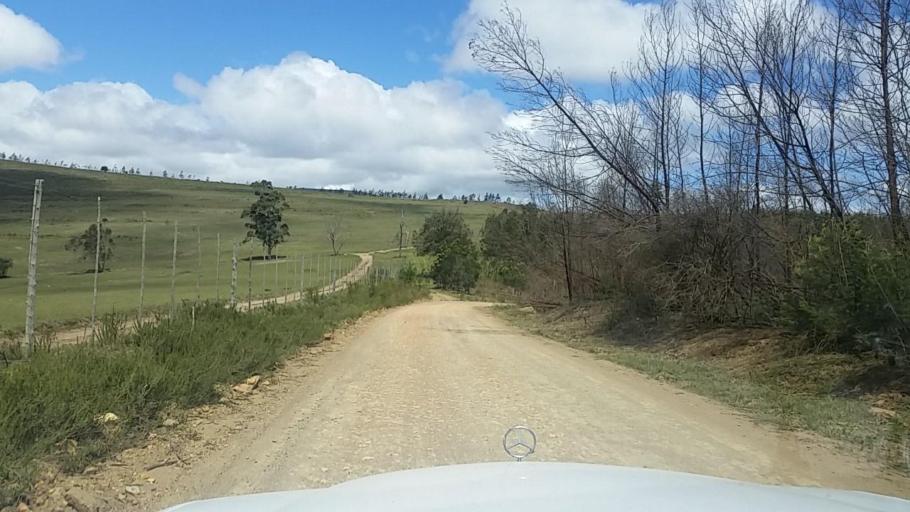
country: ZA
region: Western Cape
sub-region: Eden District Municipality
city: Knysna
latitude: -33.8582
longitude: 23.1866
